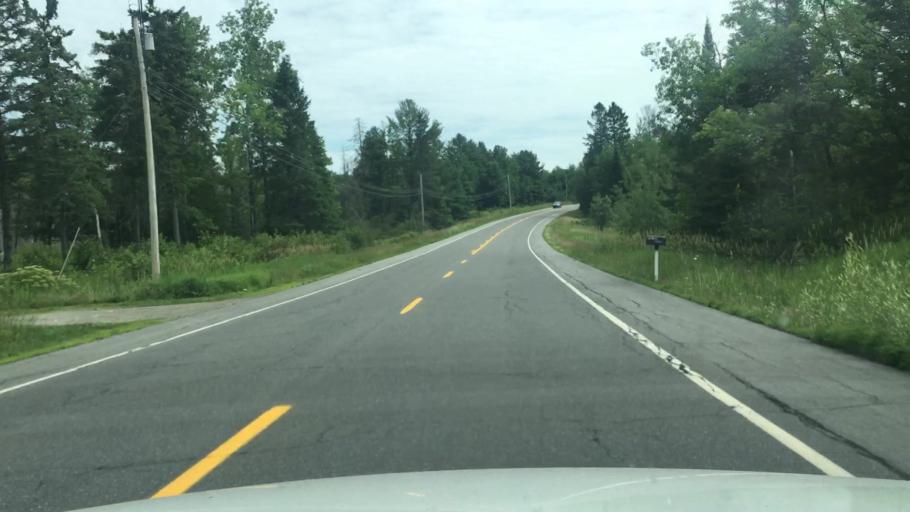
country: US
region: Maine
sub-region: Kennebec County
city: Clinton
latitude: 44.6106
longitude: -69.4441
